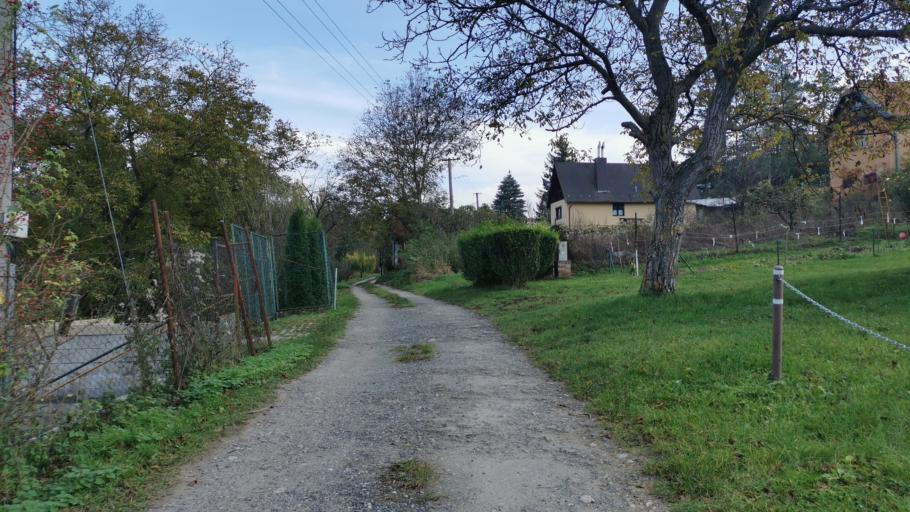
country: SK
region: Trnavsky
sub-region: Okres Skalica
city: Skalica
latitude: 48.8219
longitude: 17.2310
